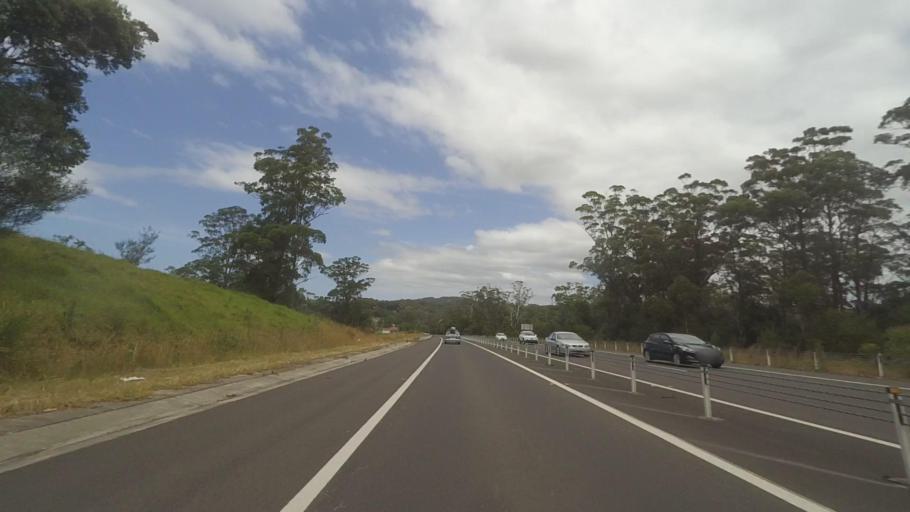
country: AU
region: New South Wales
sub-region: Shoalhaven Shire
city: Milton
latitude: -35.2103
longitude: 150.4371
